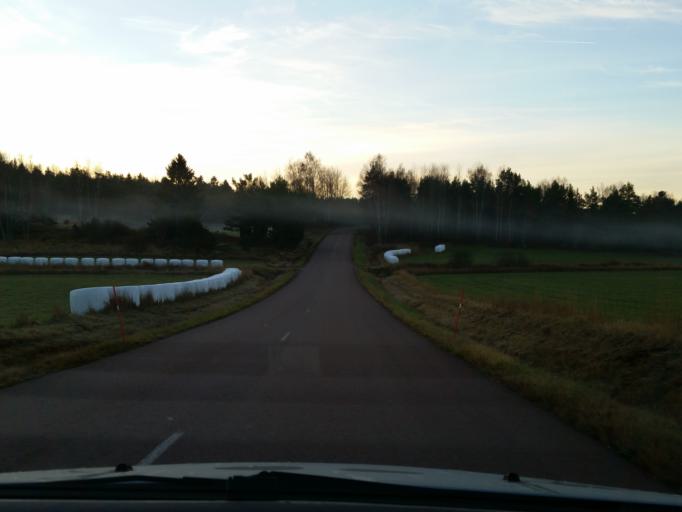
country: AX
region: Alands landsbygd
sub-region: Sund
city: Sund
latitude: 60.2216
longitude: 20.0938
